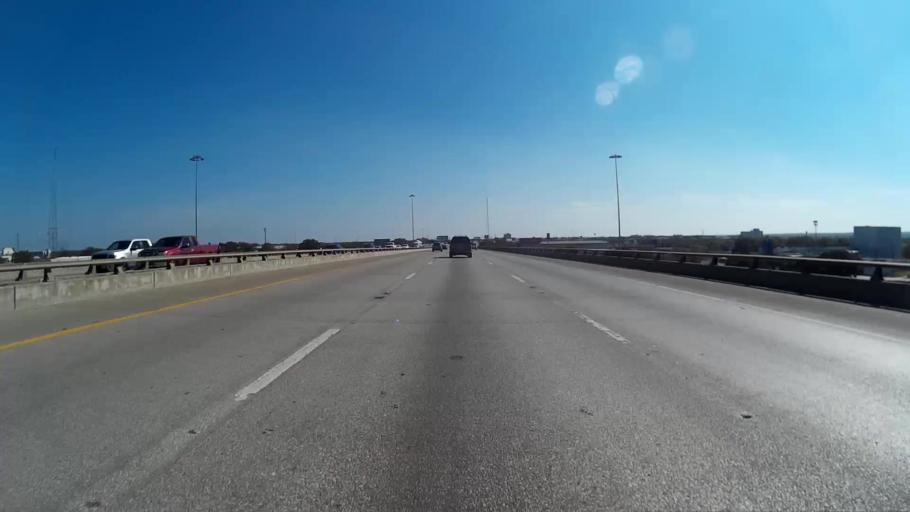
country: US
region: Texas
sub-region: Dallas County
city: Dallas
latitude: 32.7790
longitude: -96.7822
